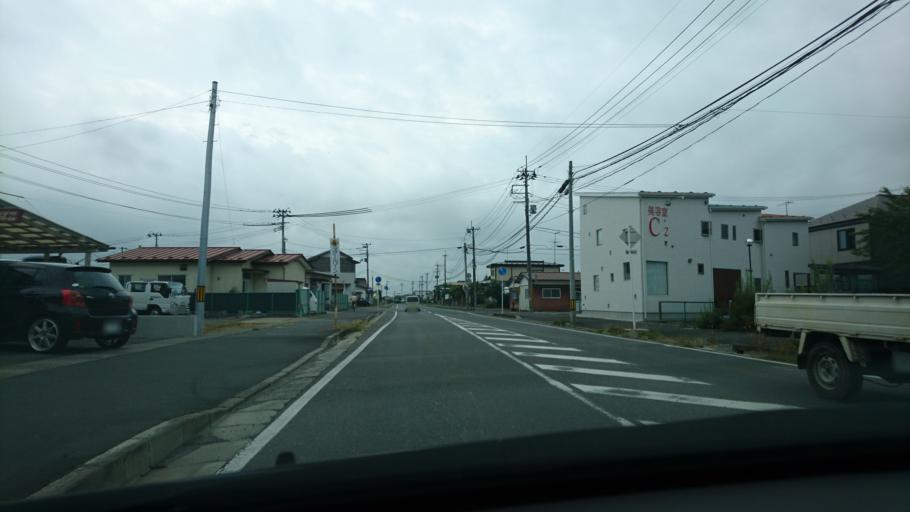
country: JP
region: Iwate
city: Ichinoseki
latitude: 38.7706
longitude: 141.1398
